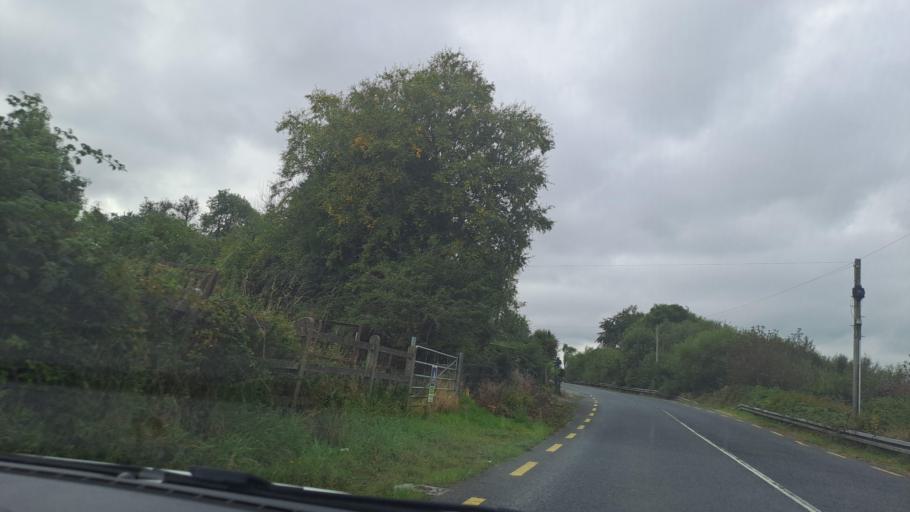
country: IE
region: Ulster
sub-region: An Cabhan
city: Bailieborough
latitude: 53.9276
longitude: -6.9339
